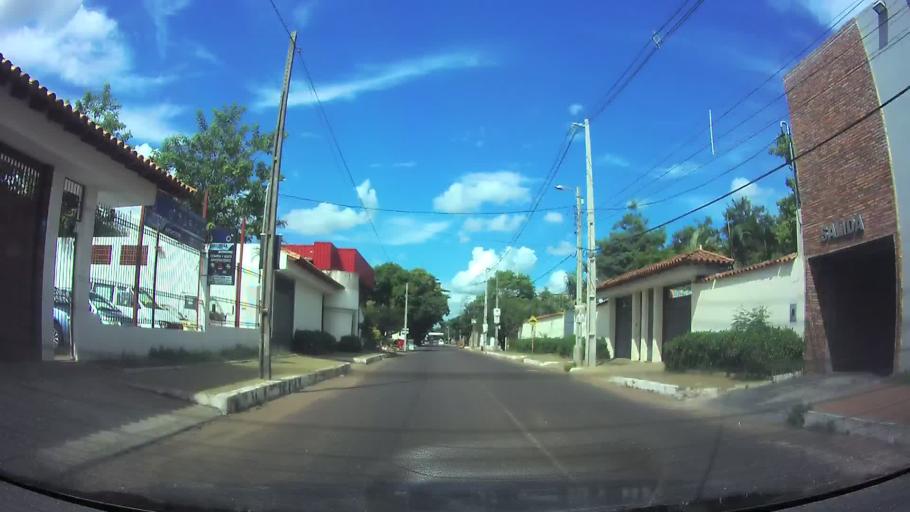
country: PY
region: Central
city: Villa Elisa
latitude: -25.3441
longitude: -57.5784
